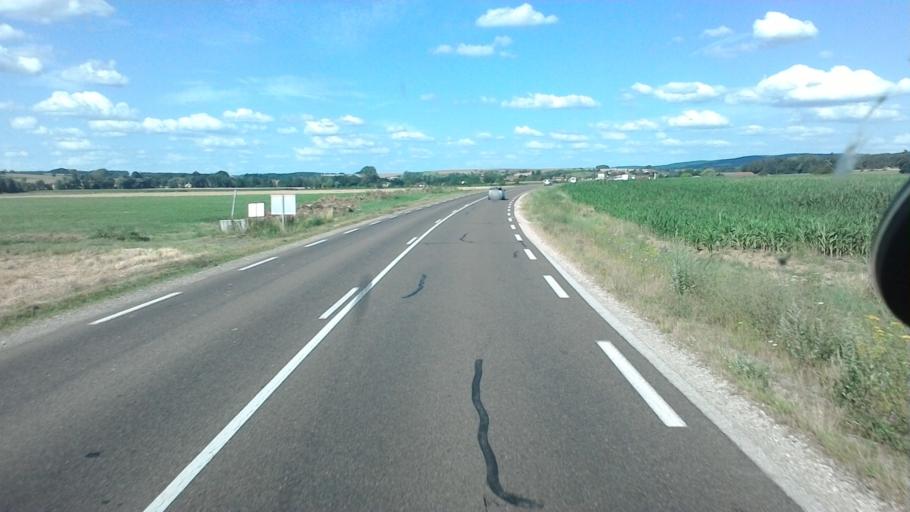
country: FR
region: Franche-Comte
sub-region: Departement de la Haute-Saone
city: Gy
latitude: 47.4185
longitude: 5.8192
